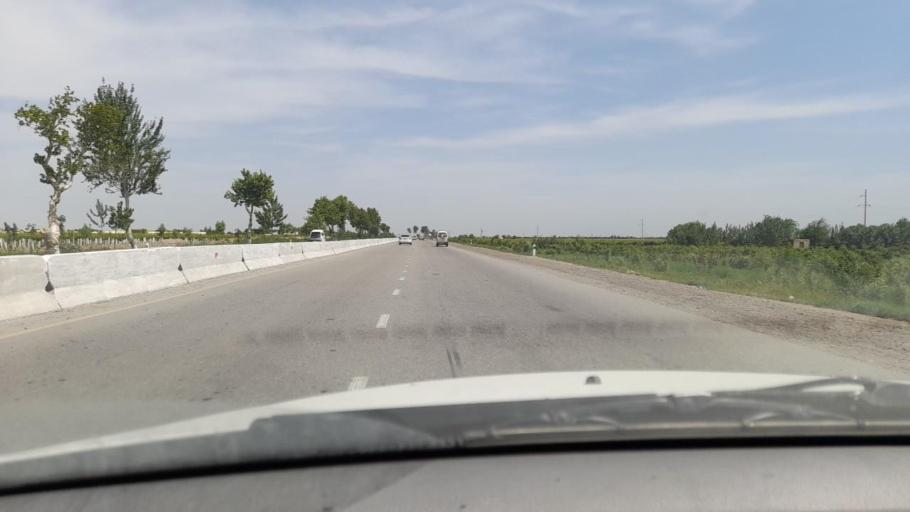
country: UZ
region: Bukhara
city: Galaosiyo
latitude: 39.8938
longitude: 64.4683
